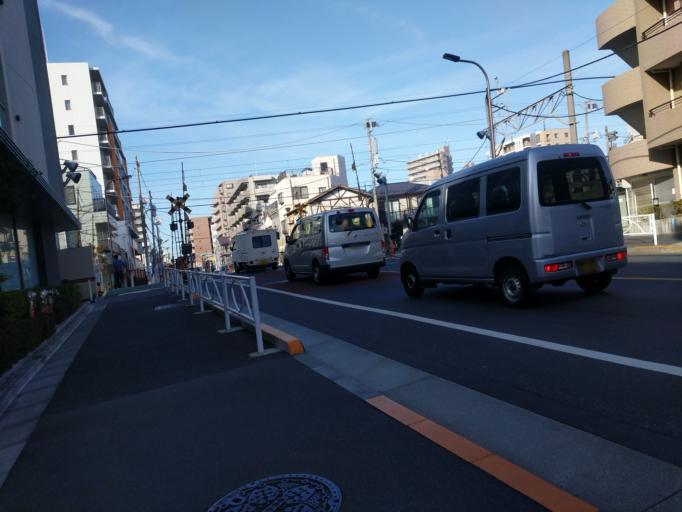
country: JP
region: Tokyo
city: Urayasu
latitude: 35.7101
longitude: 139.8268
